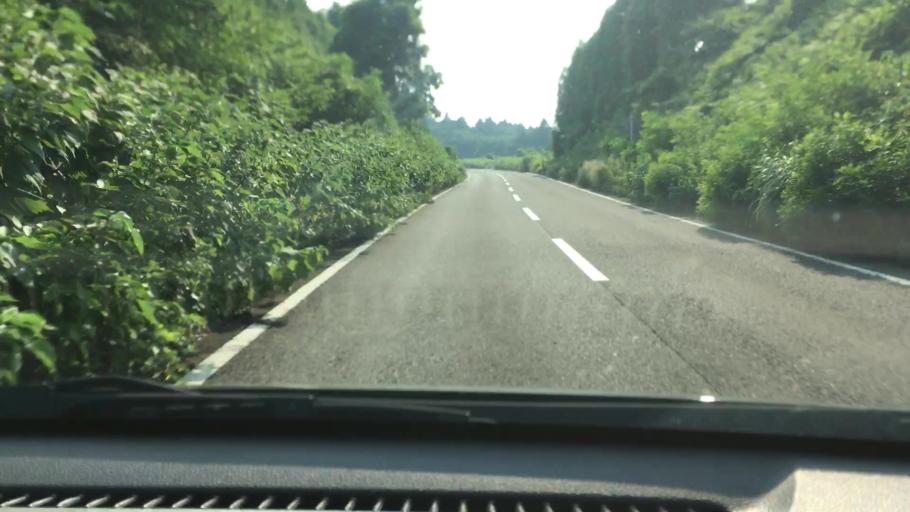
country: JP
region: Nagasaki
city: Sasebo
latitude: 33.0393
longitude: 129.6935
